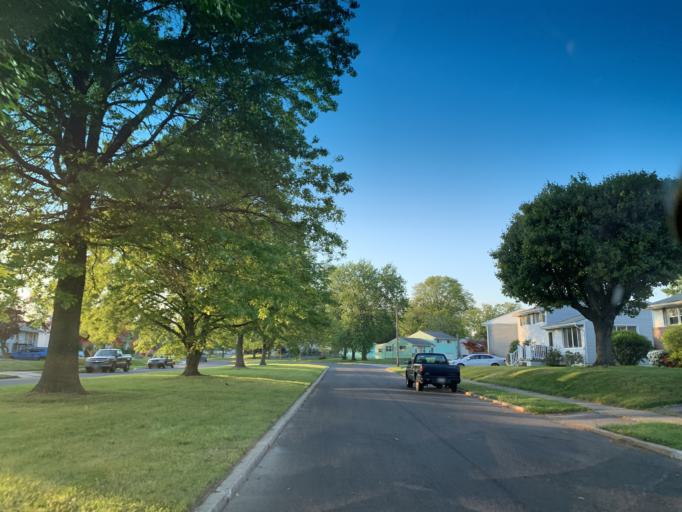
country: US
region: Maryland
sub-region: Harford County
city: Aberdeen
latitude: 39.5009
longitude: -76.1754
